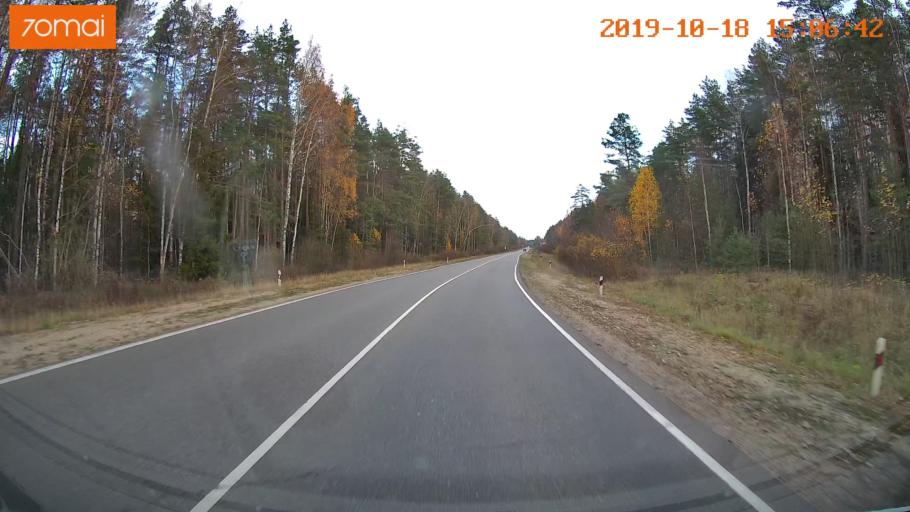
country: RU
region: Vladimir
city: Gus'-Khrustal'nyy
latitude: 55.5336
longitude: 40.5813
